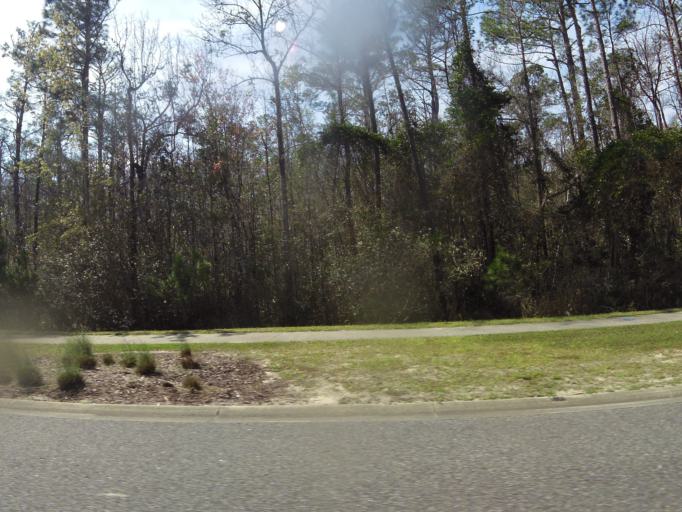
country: US
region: Florida
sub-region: Clay County
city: Middleburg
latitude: 30.0953
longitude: -81.8543
